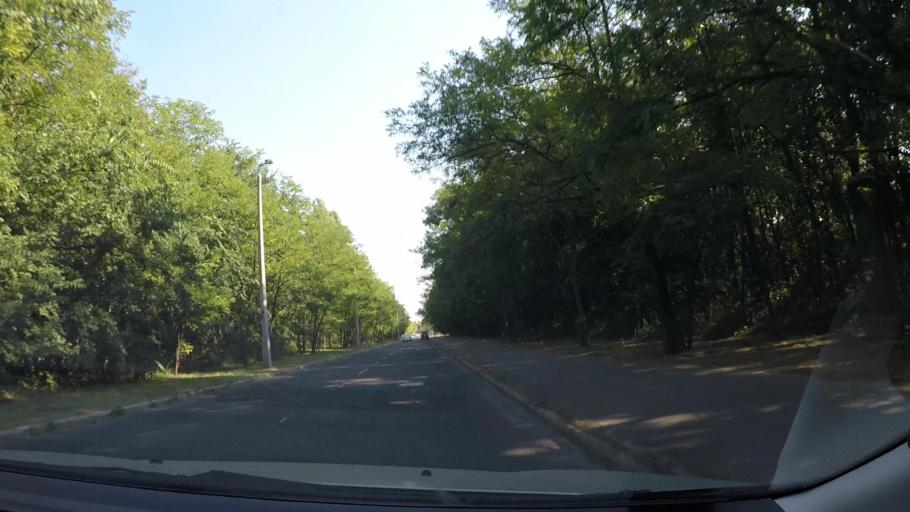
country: HU
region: Budapest
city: Budapest XV. keruelet
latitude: 47.5919
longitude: 19.1140
